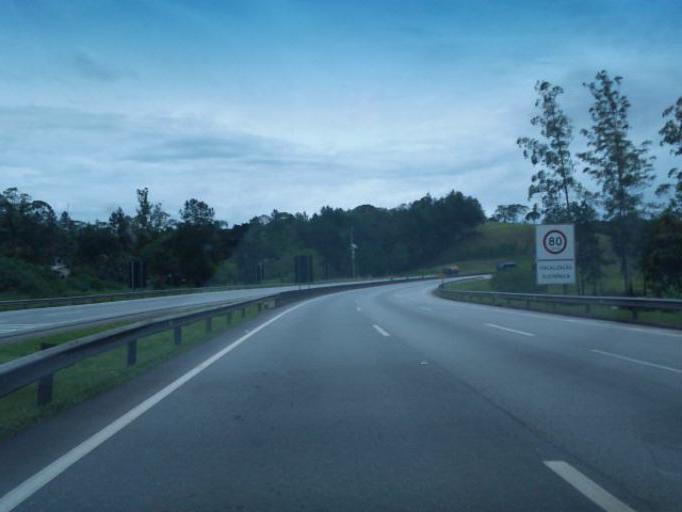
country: BR
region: Sao Paulo
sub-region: Juquitiba
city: Juquitiba
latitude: -24.0076
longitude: -47.1595
